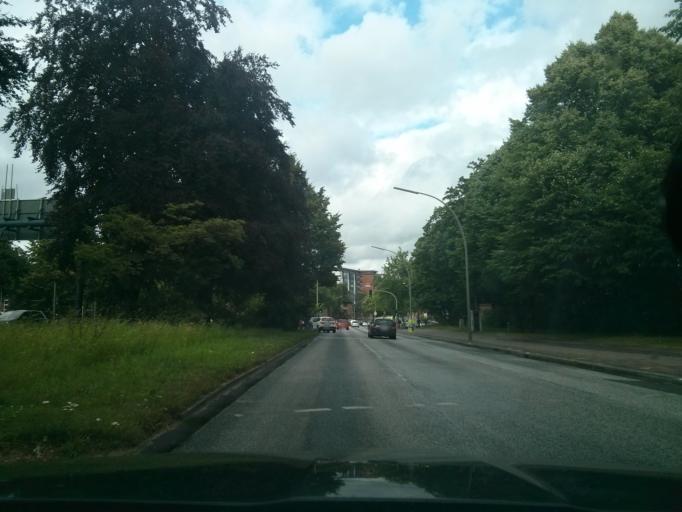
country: DE
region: Hamburg
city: Stellingen
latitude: 53.5725
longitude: 9.9431
